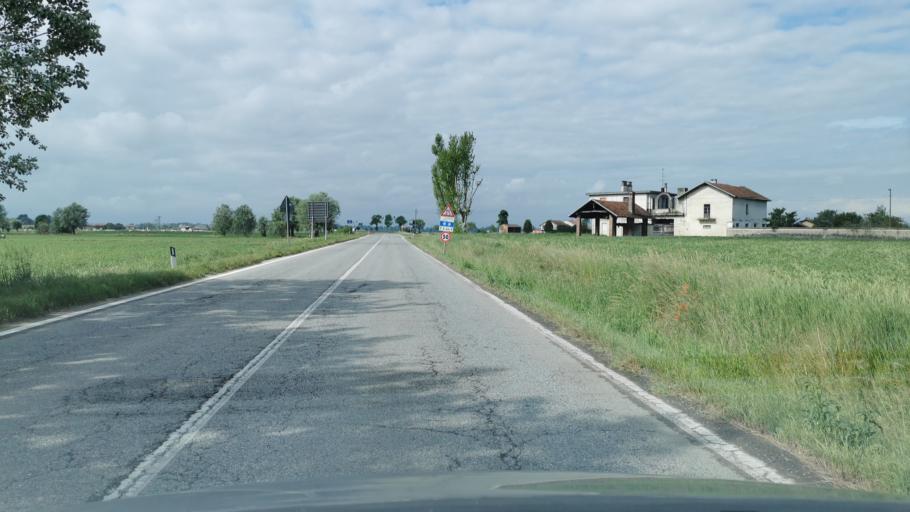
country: IT
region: Piedmont
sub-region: Provincia di Torino
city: Carmagnola
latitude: 44.8169
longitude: 7.7036
